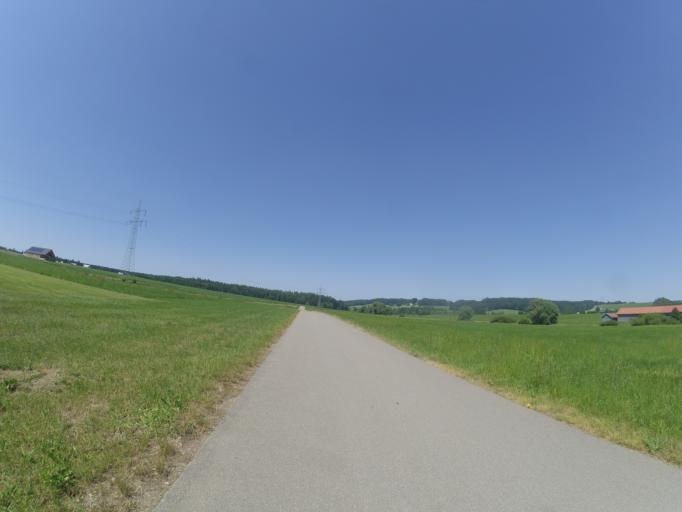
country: DE
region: Bavaria
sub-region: Swabia
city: Ottobeuren
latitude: 47.9489
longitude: 10.2901
